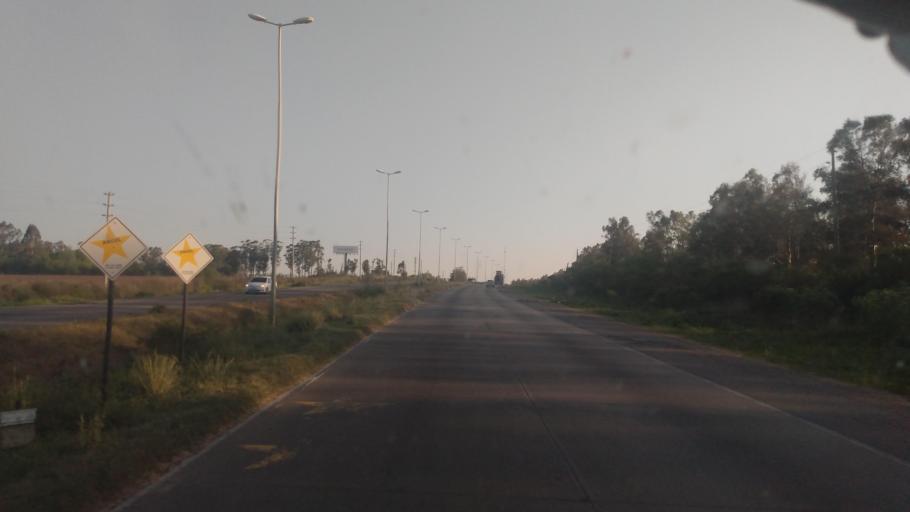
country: AR
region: Buenos Aires
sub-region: Partido de Campana
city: Campana
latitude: -34.2156
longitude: -58.9585
